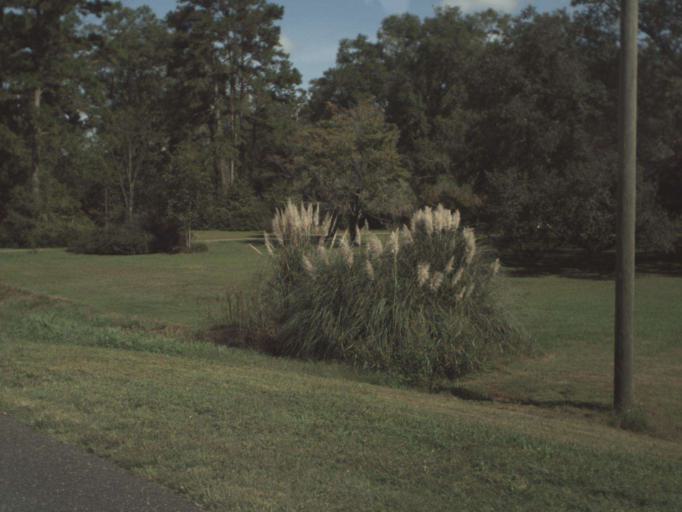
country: US
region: Florida
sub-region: Jackson County
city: Marianna
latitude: 30.8764
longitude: -85.3625
